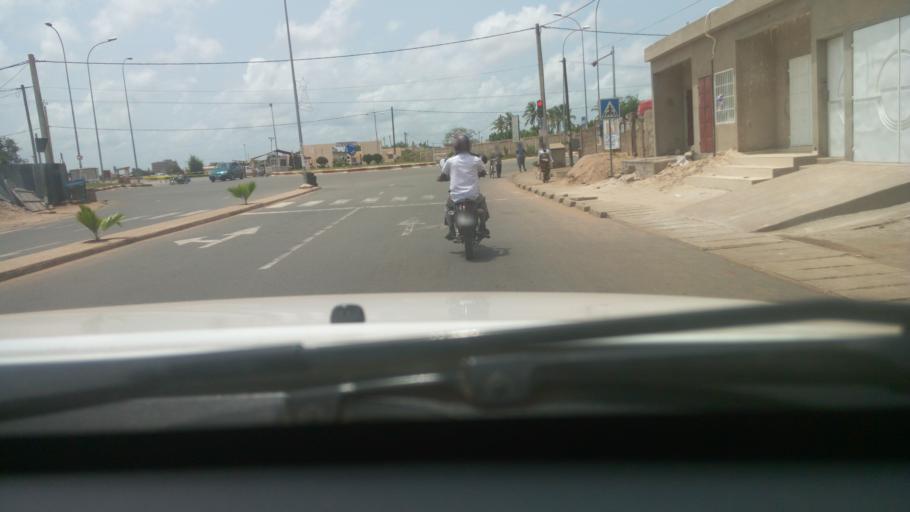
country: TG
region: Maritime
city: Lome
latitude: 6.2072
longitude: 1.1888
